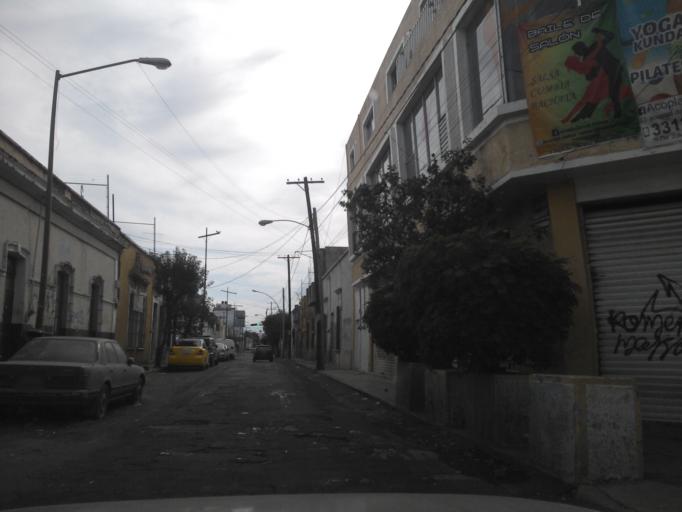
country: MX
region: Jalisco
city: Guadalajara
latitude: 20.6669
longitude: -103.3533
